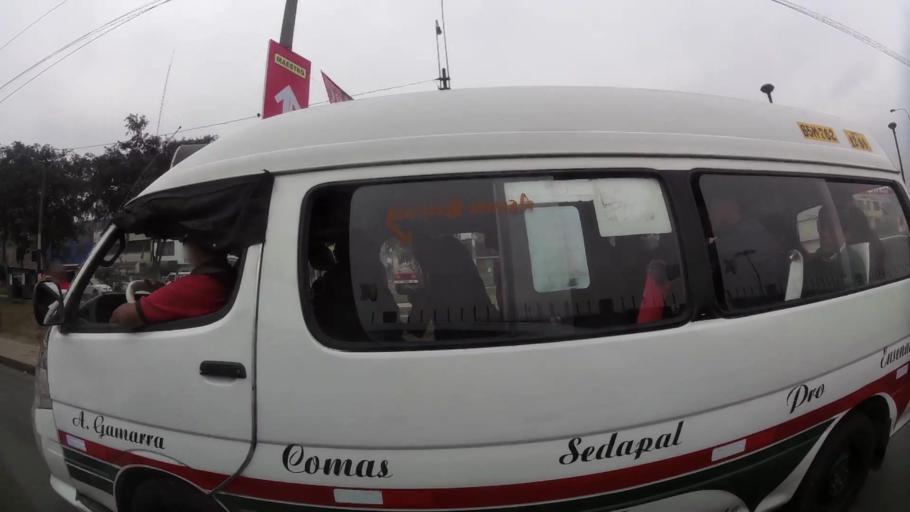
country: PE
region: Lima
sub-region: Lima
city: Independencia
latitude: -11.9821
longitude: -77.0584
